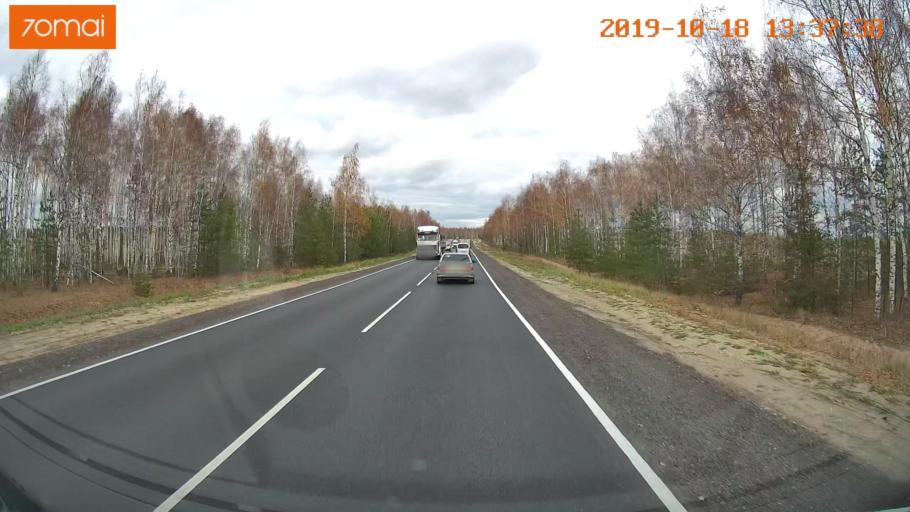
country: RU
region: Rjazan
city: Solotcha
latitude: 54.8812
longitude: 39.9972
